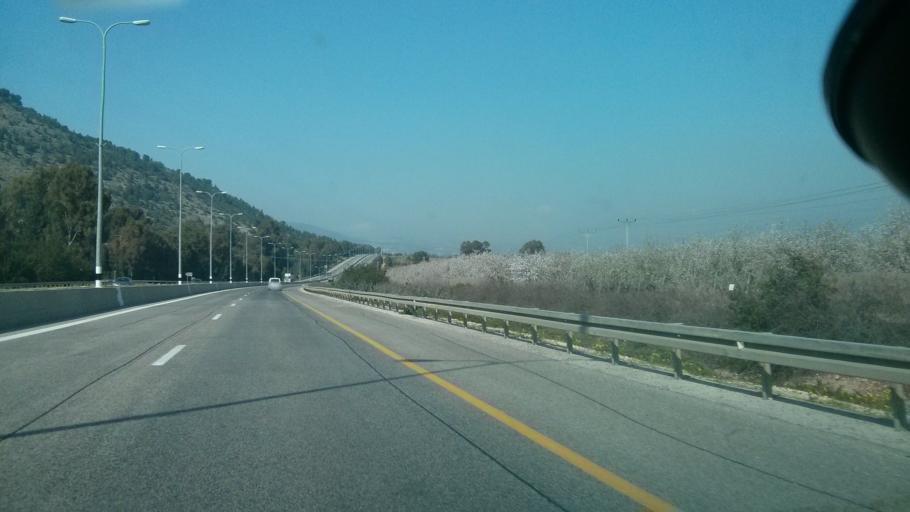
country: IL
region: Northern District
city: Rosh Pinna
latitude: 33.0792
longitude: 35.5754
